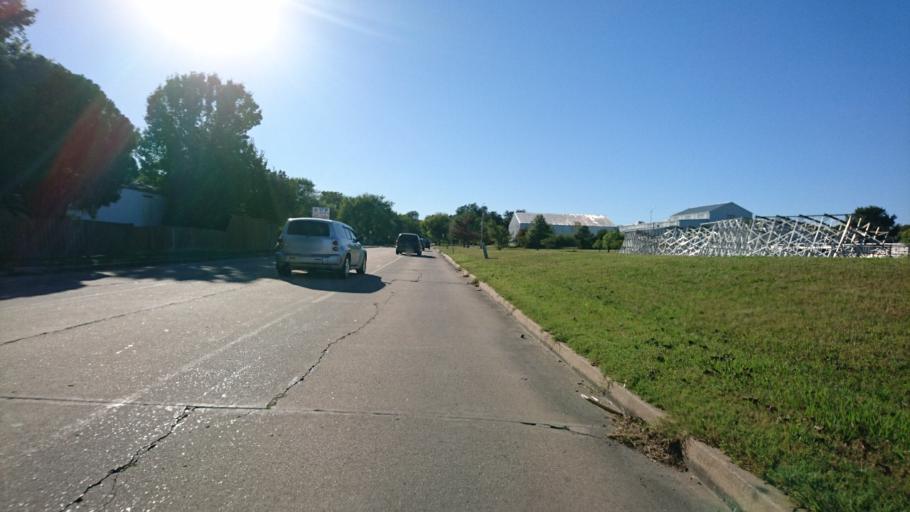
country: US
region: Oklahoma
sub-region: Rogers County
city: Claremore
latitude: 36.3110
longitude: -95.6289
